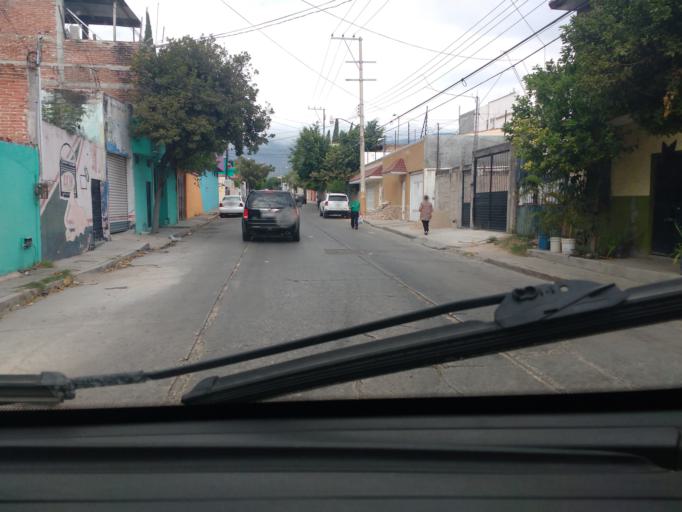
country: MX
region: Chiapas
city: Tuxtla Gutierrez
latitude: 16.7596
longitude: -93.1113
